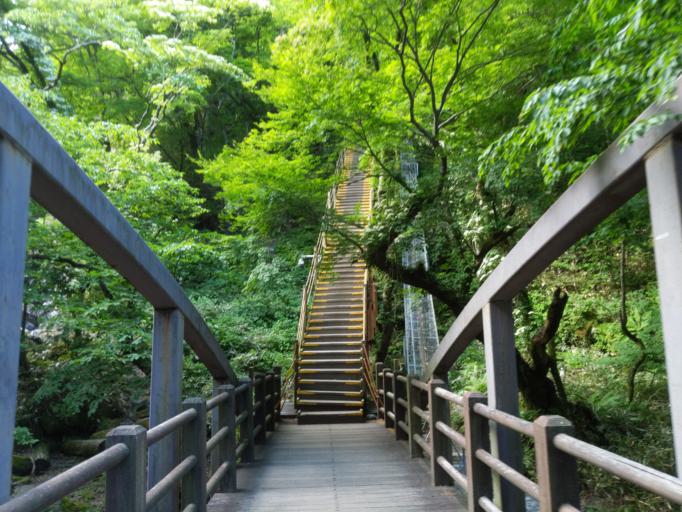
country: KR
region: Jeju-do
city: Jeju-si
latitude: 33.4011
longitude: 126.5402
